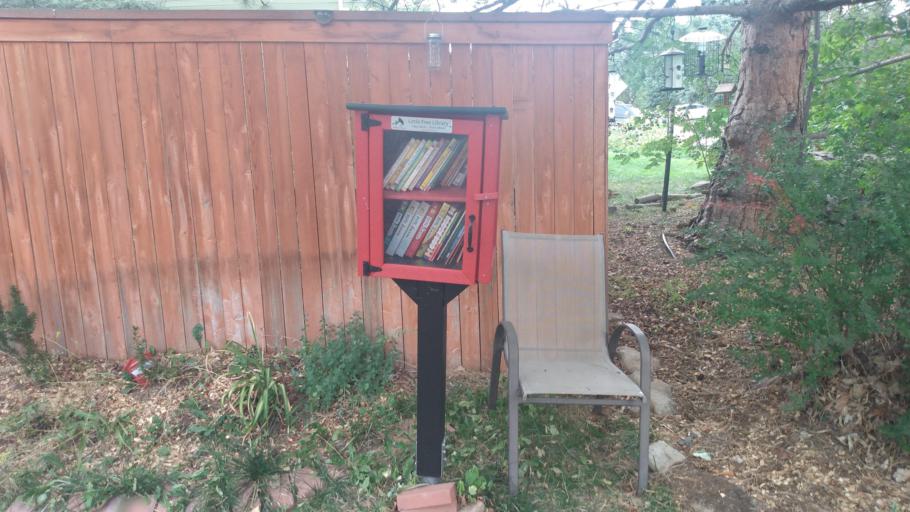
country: US
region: Colorado
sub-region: Boulder County
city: Louisville
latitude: 39.9764
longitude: -105.1475
